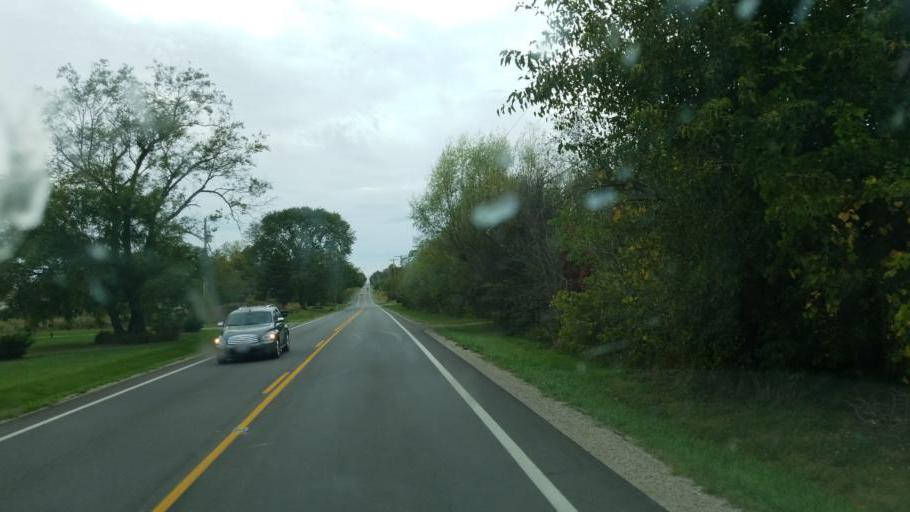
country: US
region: Ohio
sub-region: Lorain County
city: South Amherst
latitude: 41.3457
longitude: -82.2825
